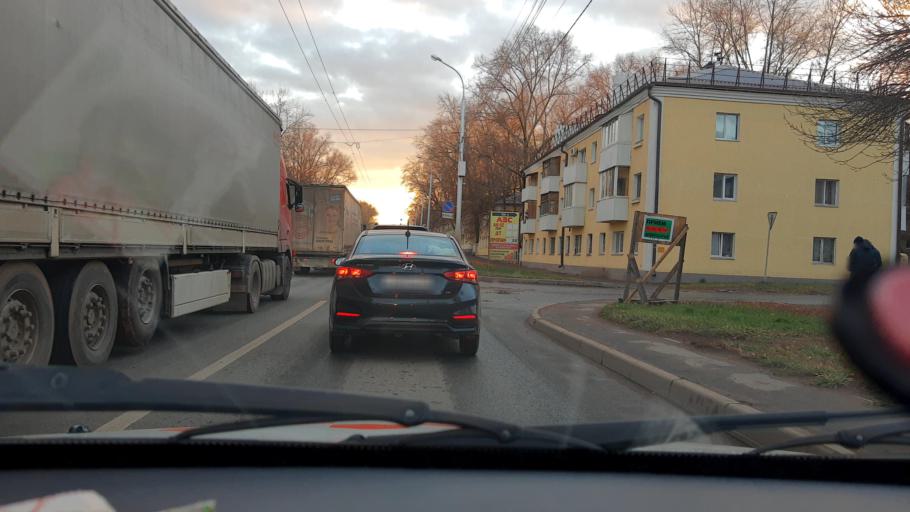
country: RU
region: Bashkortostan
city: Ufa
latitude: 54.8256
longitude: 56.1132
